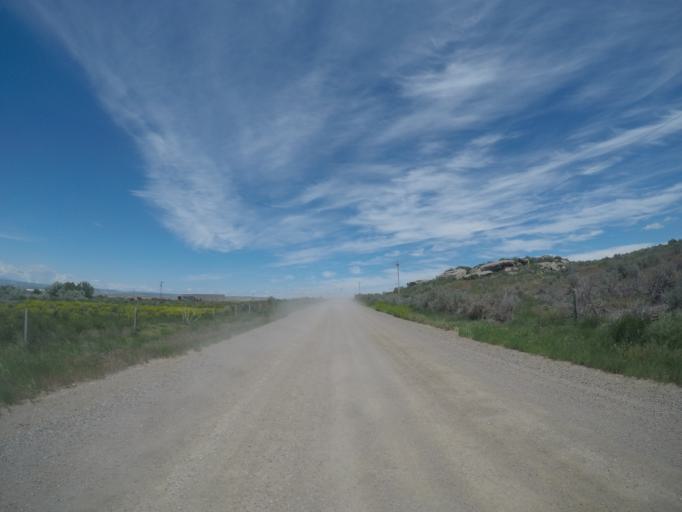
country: US
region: Montana
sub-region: Carbon County
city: Red Lodge
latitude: 45.2449
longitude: -108.8639
